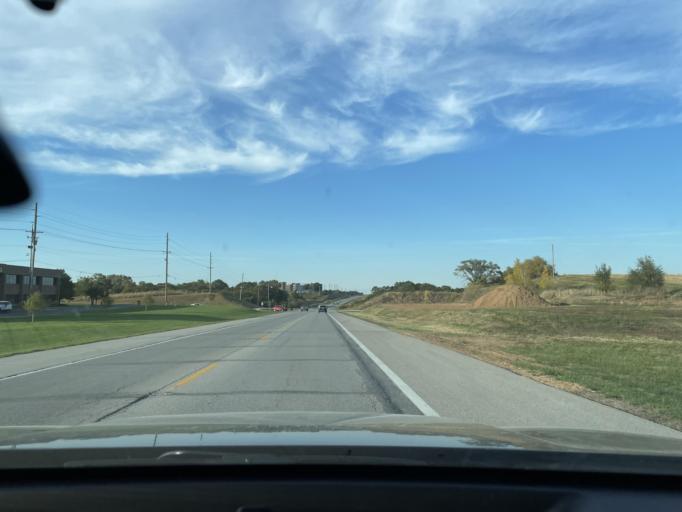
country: US
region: Missouri
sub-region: Buchanan County
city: Saint Joseph
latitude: 39.7614
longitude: -94.7685
